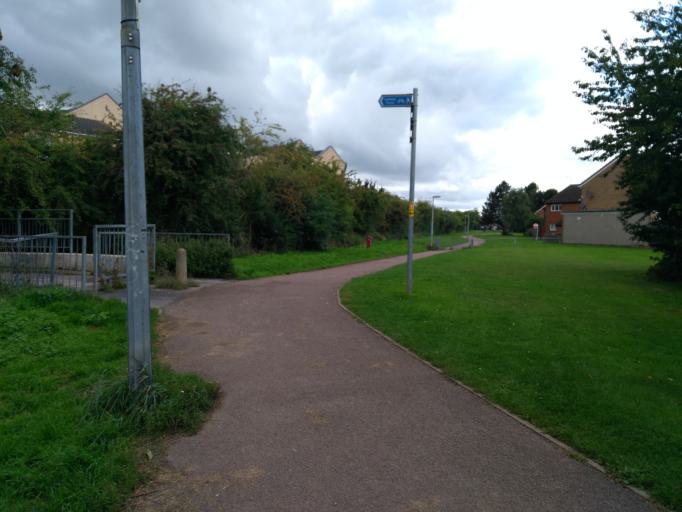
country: GB
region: England
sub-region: Central Bedfordshire
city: Houghton Regis
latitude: 51.9058
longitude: -0.4991
